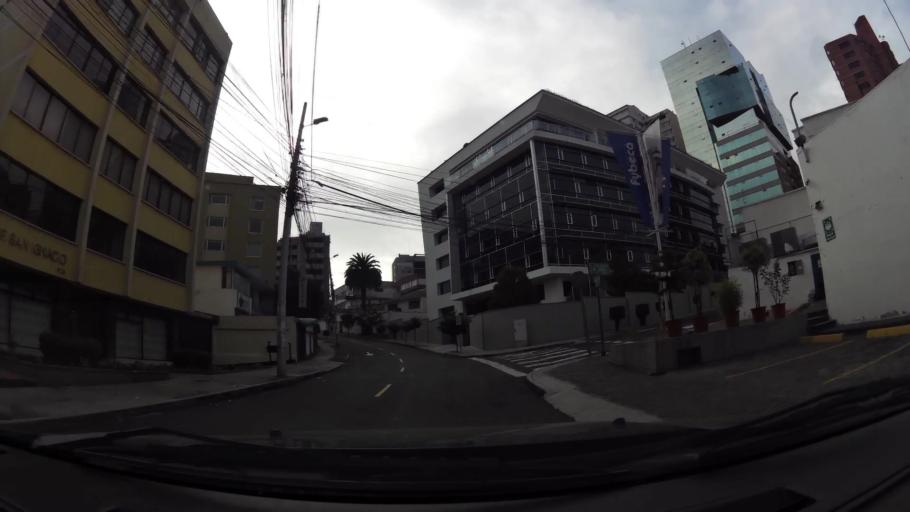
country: EC
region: Pichincha
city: Quito
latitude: -0.2017
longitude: -78.4826
